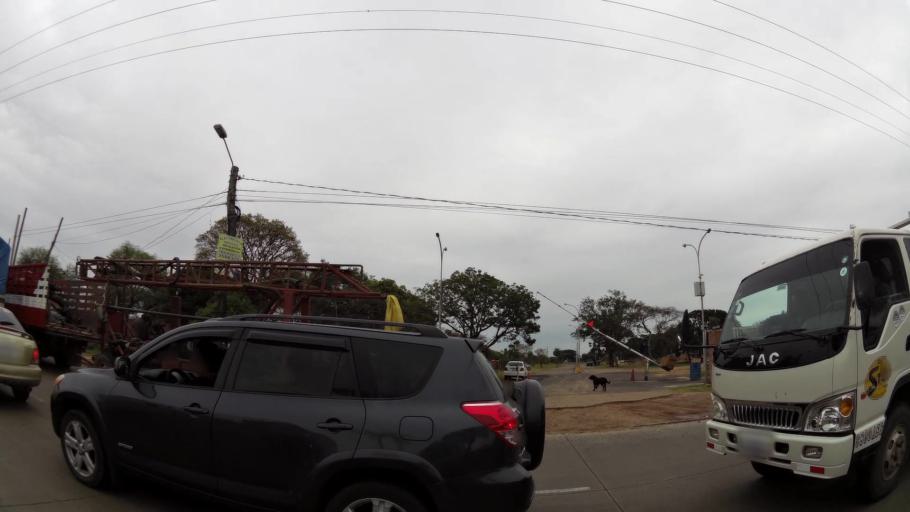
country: BO
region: Santa Cruz
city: Santa Cruz de la Sierra
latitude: -17.8229
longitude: -63.1852
